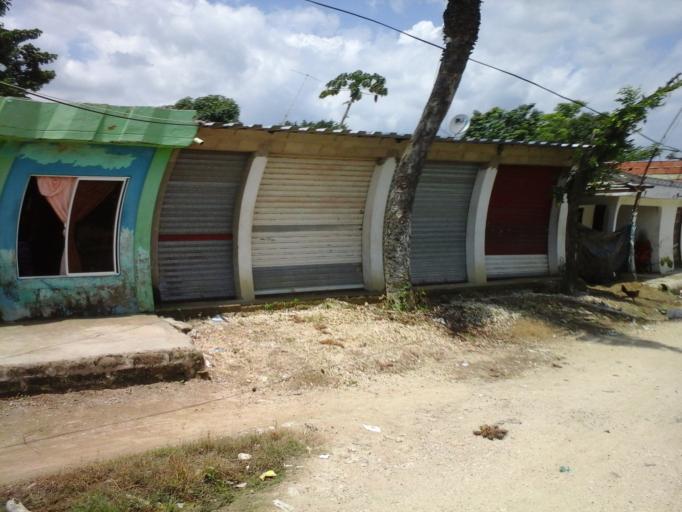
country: CO
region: Bolivar
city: San Pablo
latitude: 10.1446
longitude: -75.2772
